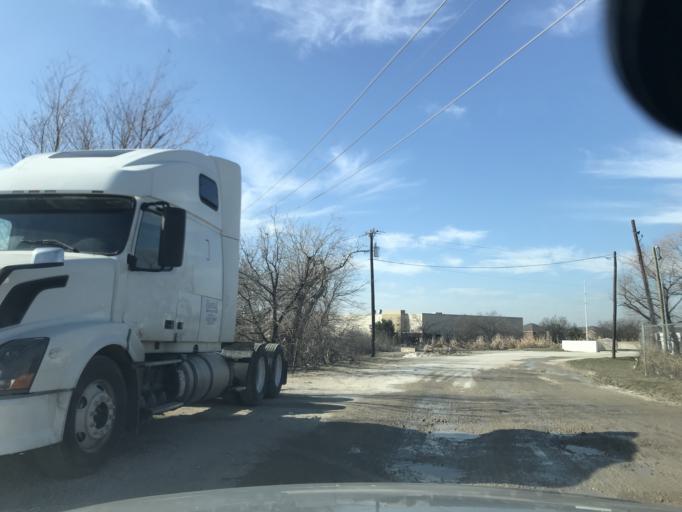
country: US
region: Texas
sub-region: Denton County
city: The Colony
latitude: 33.0834
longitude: -96.8551
